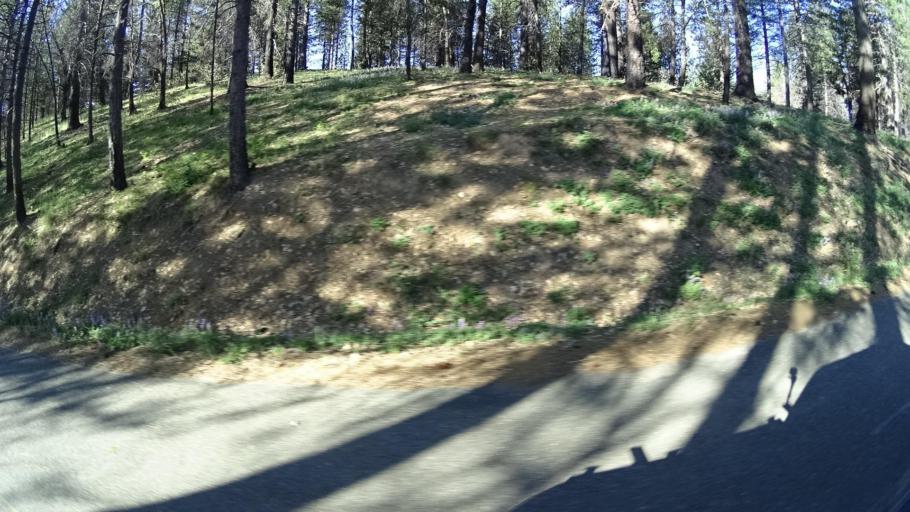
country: US
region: California
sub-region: Lake County
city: Upper Lake
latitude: 39.3099
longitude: -122.9402
